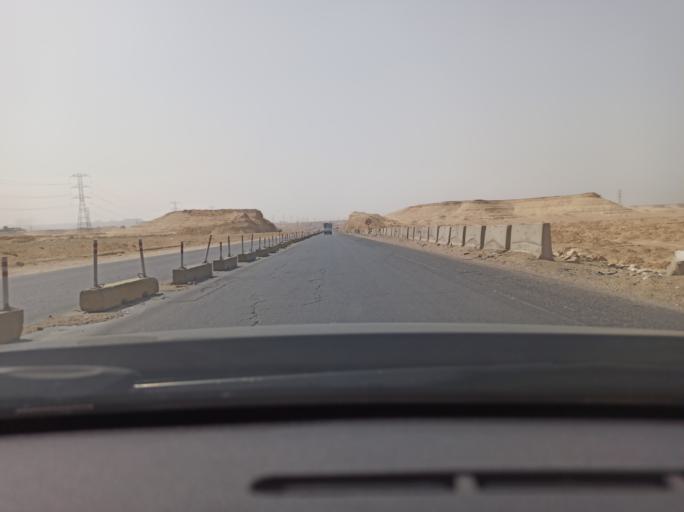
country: EG
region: Muhafazat Bani Suwayf
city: Bush
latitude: 29.1766
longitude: 31.2442
